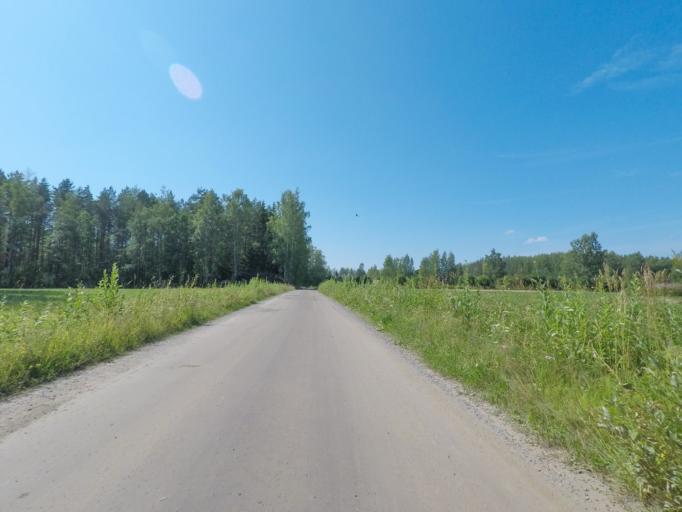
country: FI
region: Southern Savonia
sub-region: Mikkeli
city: Puumala
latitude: 61.4278
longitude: 28.0189
